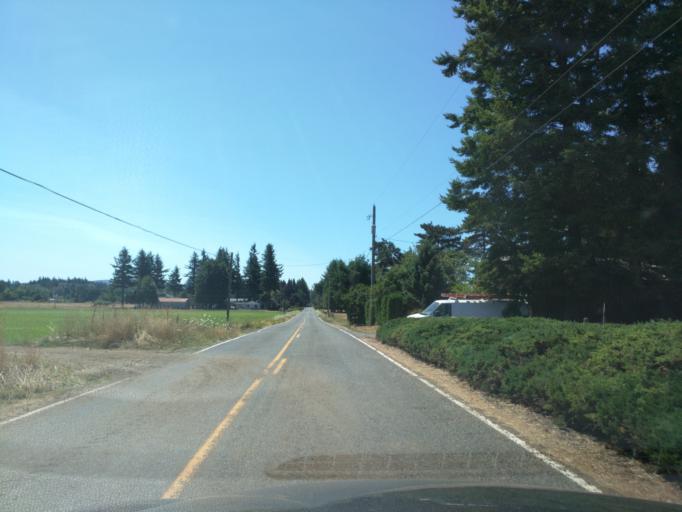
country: US
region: Washington
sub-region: Whatcom County
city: Lynden
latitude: 48.8846
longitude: -122.4145
